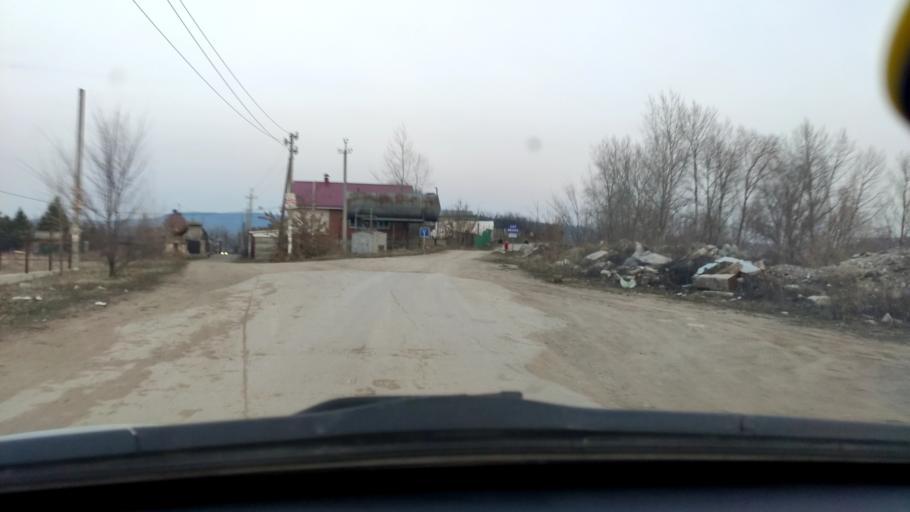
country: RU
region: Samara
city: Zhigulevsk
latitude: 53.4553
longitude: 49.5177
